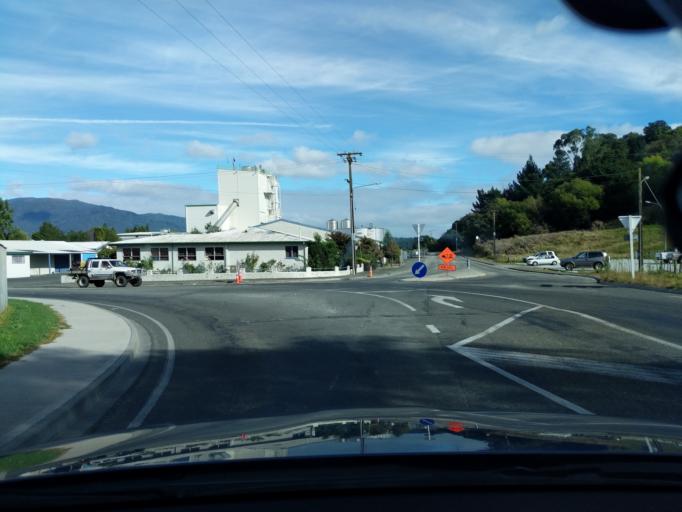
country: NZ
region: Tasman
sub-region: Tasman District
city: Takaka
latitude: -40.8552
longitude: 172.8164
